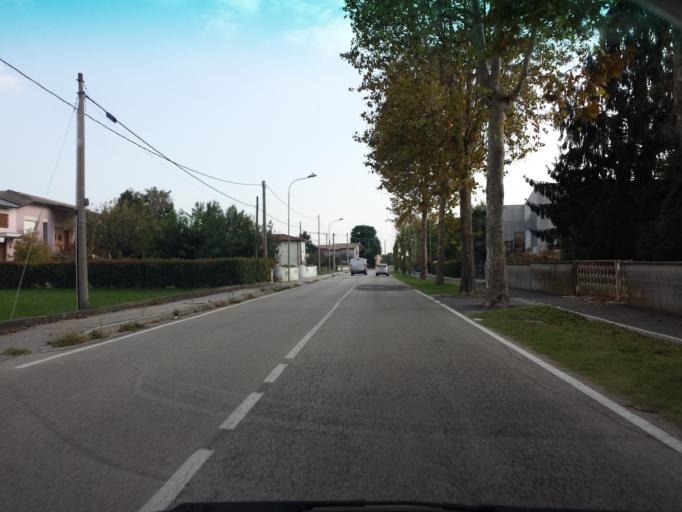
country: IT
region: Veneto
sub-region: Provincia di Vicenza
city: Dueville
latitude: 45.6256
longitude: 11.5531
